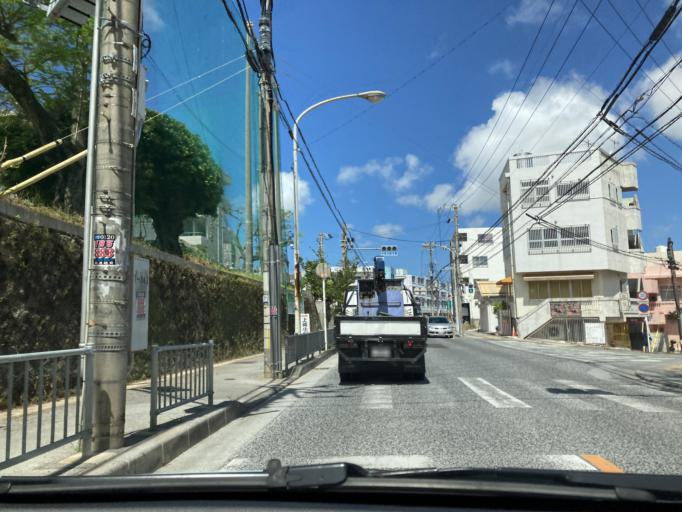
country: JP
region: Okinawa
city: Naha-shi
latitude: 26.2002
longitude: 127.7005
